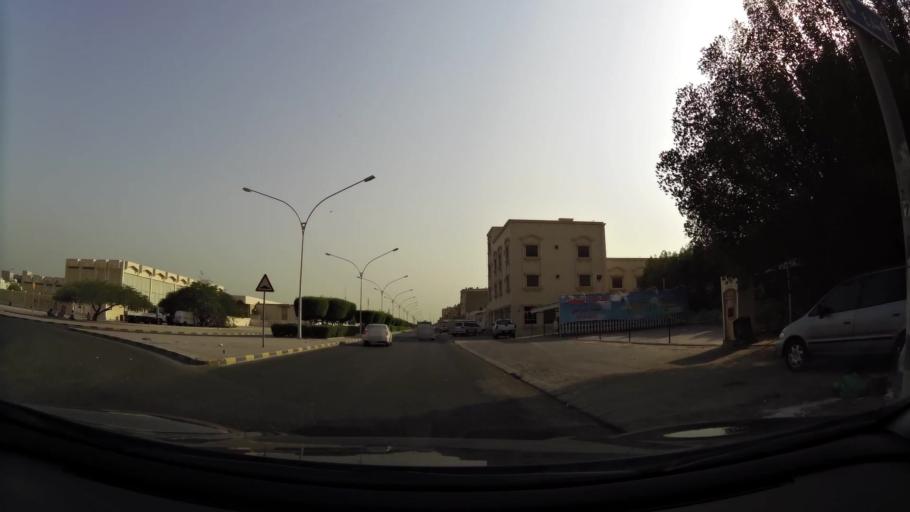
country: KW
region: Al Ahmadi
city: Ar Riqqah
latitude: 29.1158
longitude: 48.1053
